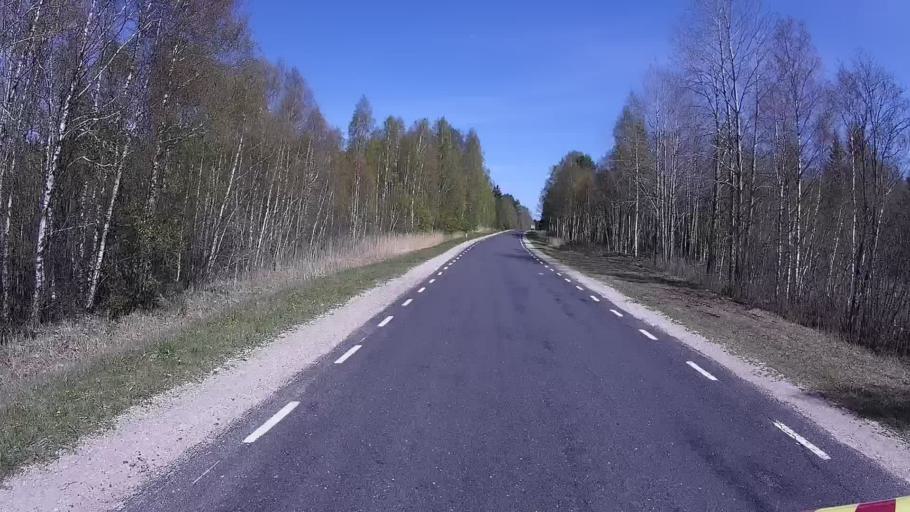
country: EE
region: Laeaene
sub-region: Ridala Parish
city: Uuemoisa
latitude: 59.0236
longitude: 23.8049
